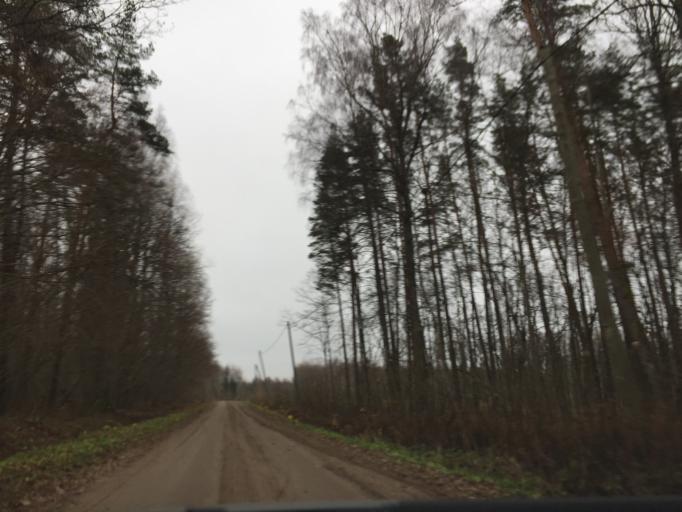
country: LV
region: Limbazu Rajons
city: Limbazi
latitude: 57.5047
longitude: 24.7617
